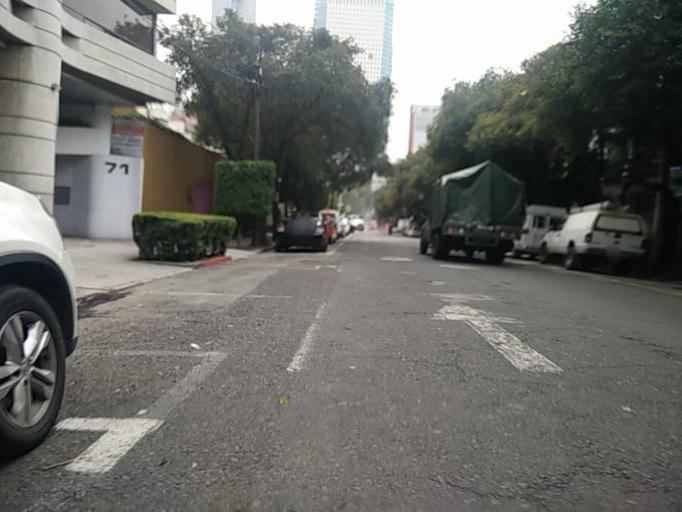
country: MX
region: Mexico City
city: Miguel Hidalgo
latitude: 19.4285
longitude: -99.1772
